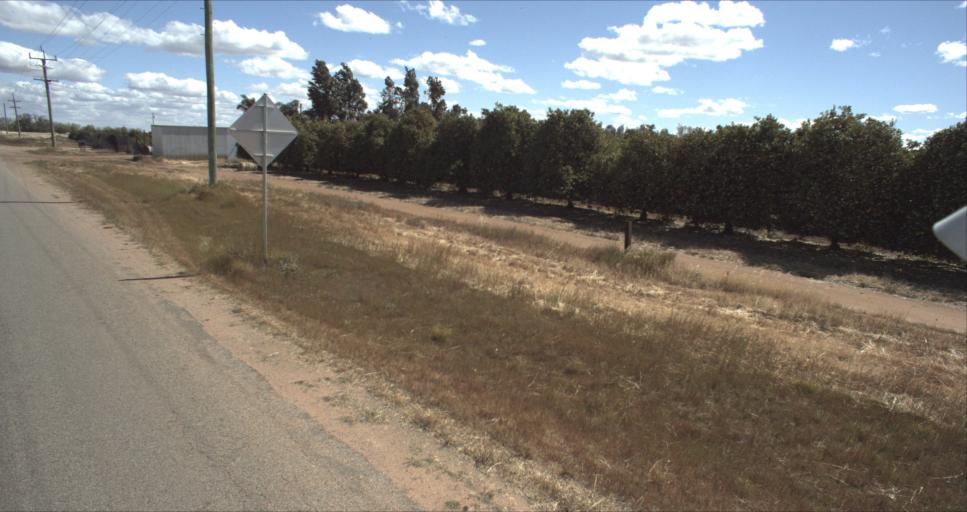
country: AU
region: New South Wales
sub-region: Leeton
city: Leeton
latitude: -34.5103
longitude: 146.2536
